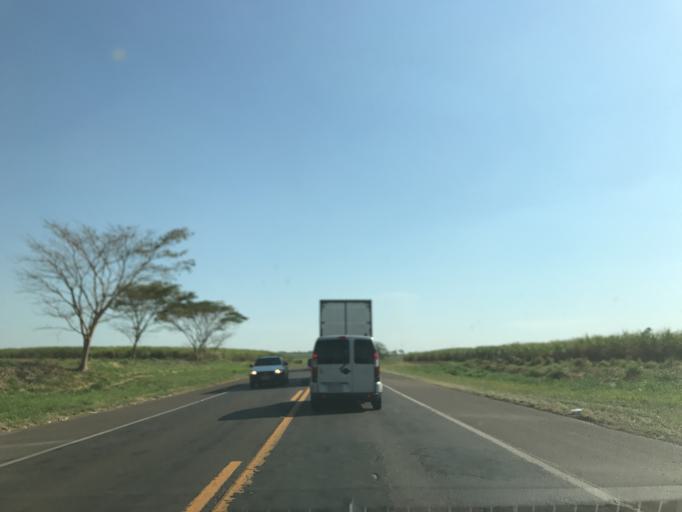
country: BR
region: Sao Paulo
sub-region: Penapolis
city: Penapolis
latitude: -21.4806
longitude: -50.2032
